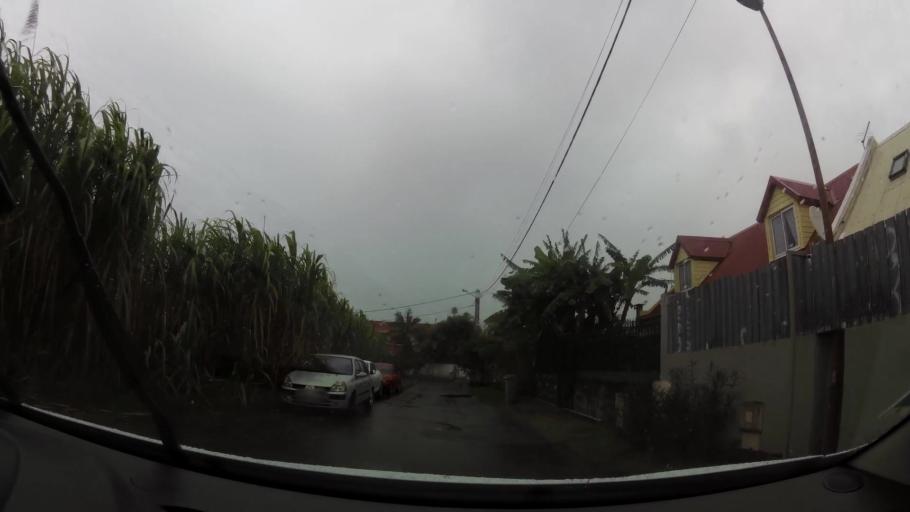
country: RE
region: Reunion
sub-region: Reunion
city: Saint-Andre
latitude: -20.9616
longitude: 55.6446
